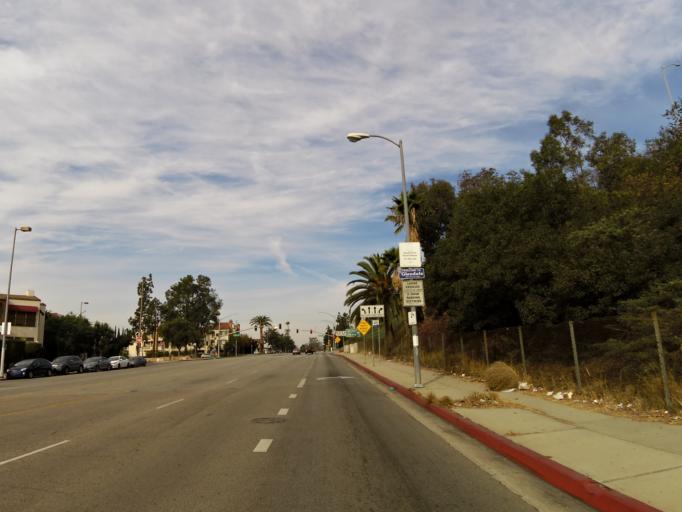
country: US
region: California
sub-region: Los Angeles County
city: Glendale
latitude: 34.1458
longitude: -118.2284
